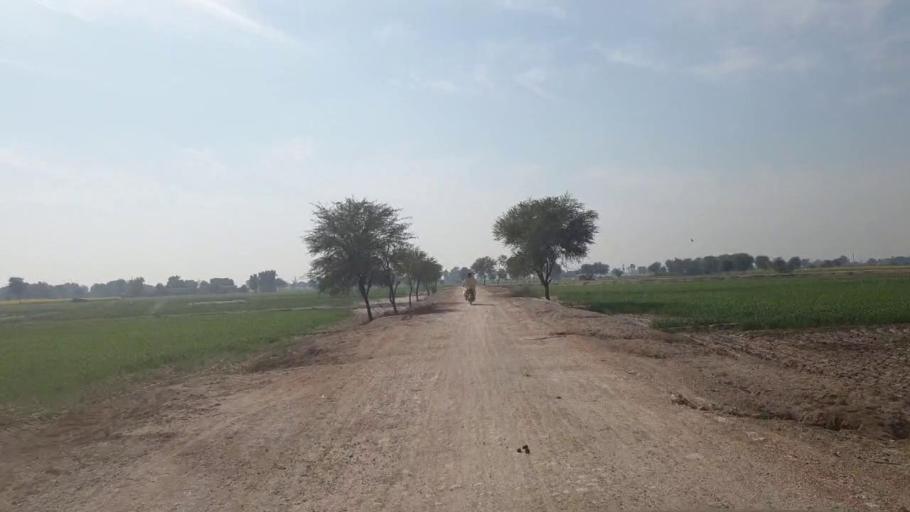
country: PK
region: Sindh
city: Nawabshah
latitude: 26.1629
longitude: 68.5095
